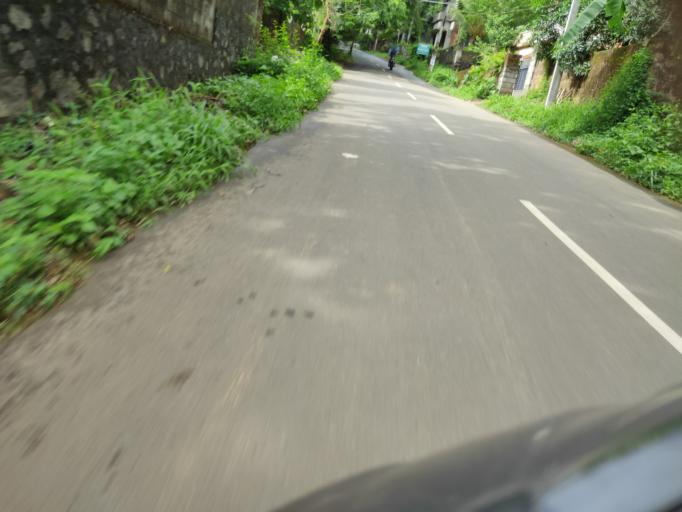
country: IN
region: Kerala
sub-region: Malappuram
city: Manjeri
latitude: 11.1360
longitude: 76.1296
